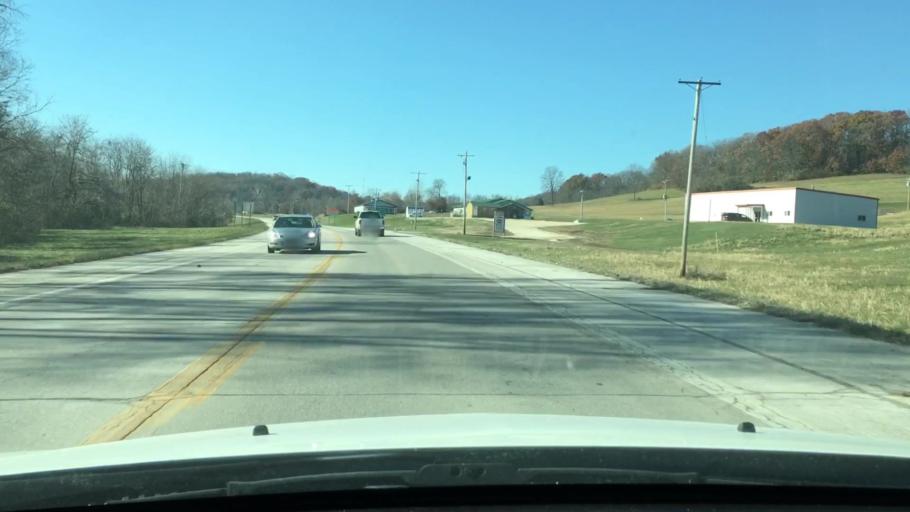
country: US
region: Missouri
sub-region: Pike County
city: Louisiana
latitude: 39.4517
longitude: -91.0630
